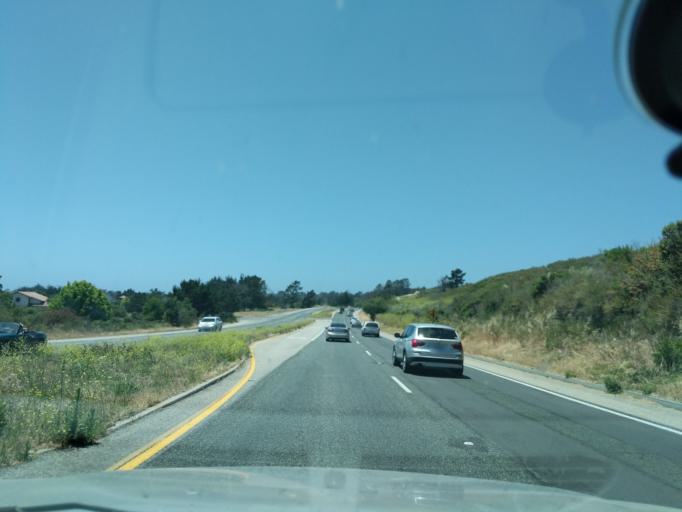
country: US
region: California
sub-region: Monterey County
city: Carmel-by-the-Sea
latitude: 36.5426
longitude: -121.8904
